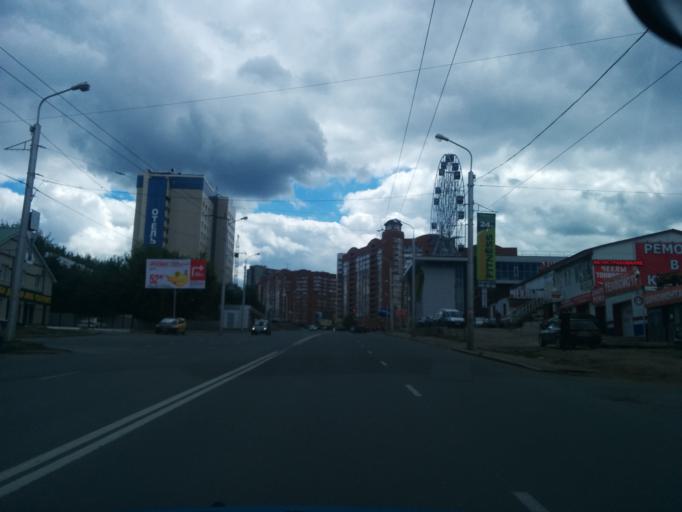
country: RU
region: Bashkortostan
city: Ufa
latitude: 54.7156
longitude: 55.9944
